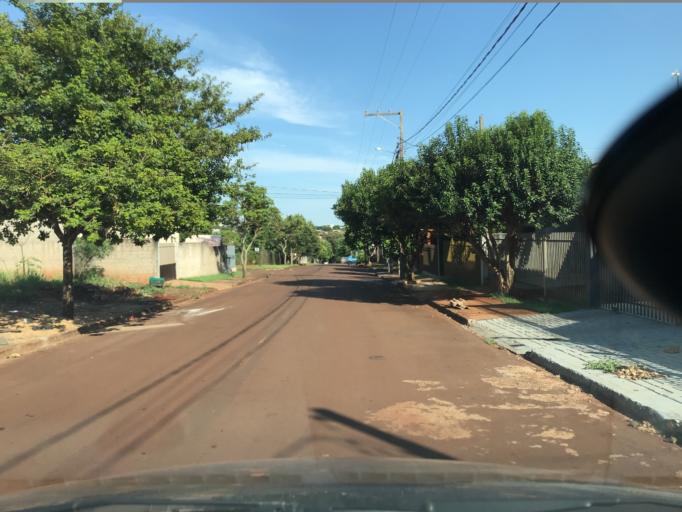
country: BR
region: Parana
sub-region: Palotina
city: Palotina
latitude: -24.2907
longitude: -53.8274
